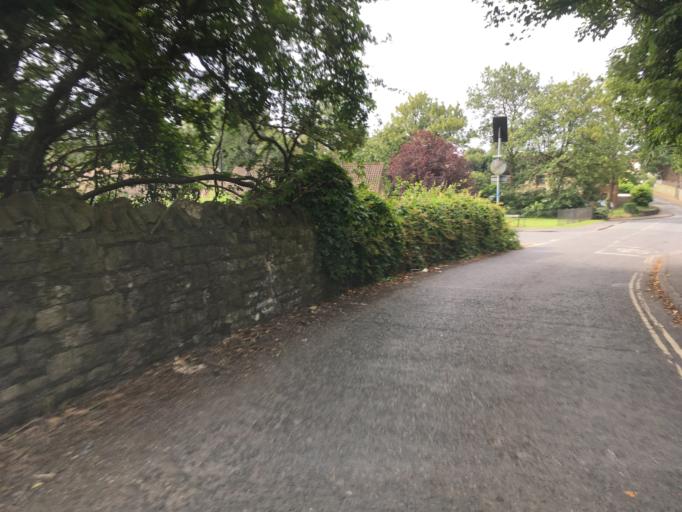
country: GB
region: England
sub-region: South Gloucestershire
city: Mangotsfield
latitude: 51.4783
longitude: -2.5229
